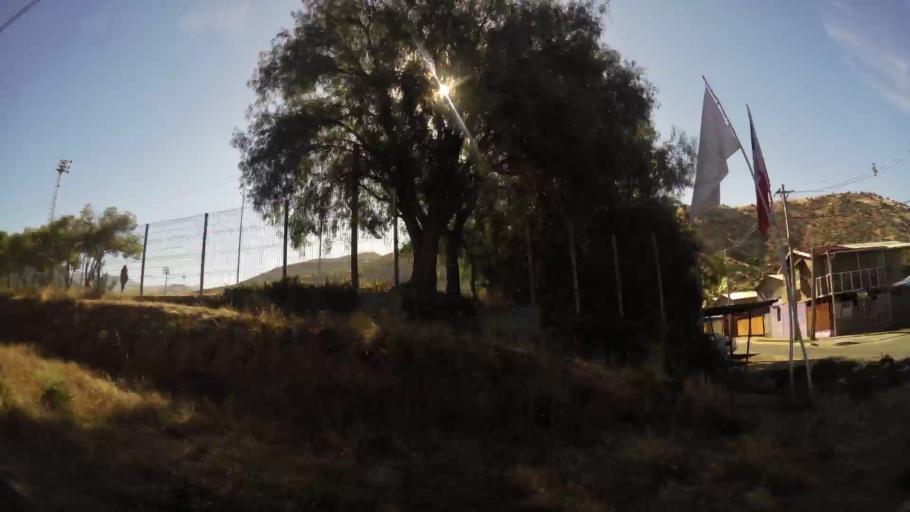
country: CL
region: Santiago Metropolitan
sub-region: Provincia de Chacabuco
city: Lampa
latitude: -33.3925
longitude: -71.1207
